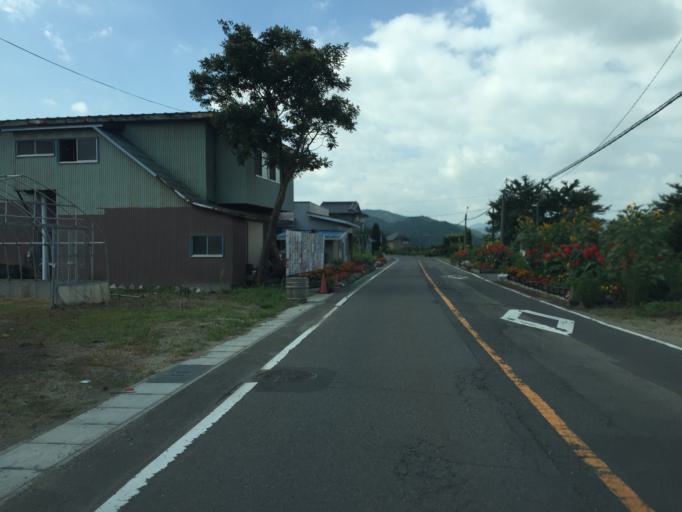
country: JP
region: Fukushima
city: Inawashiro
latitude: 37.4222
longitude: 140.1454
